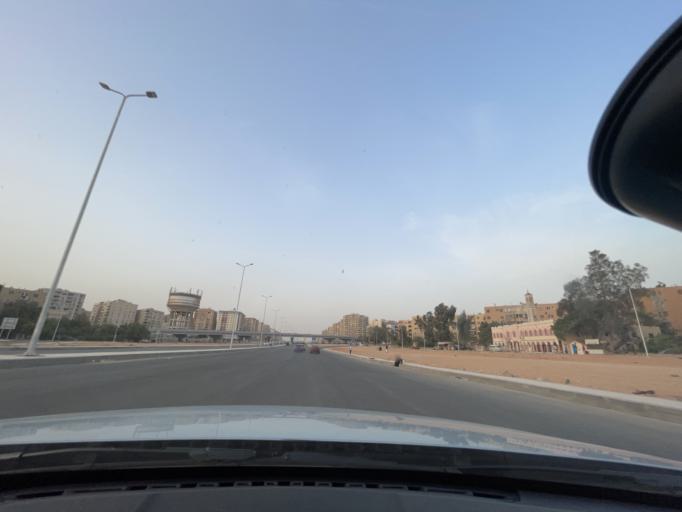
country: EG
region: Muhafazat al Qahirah
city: Cairo
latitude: 30.0455
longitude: 31.3640
